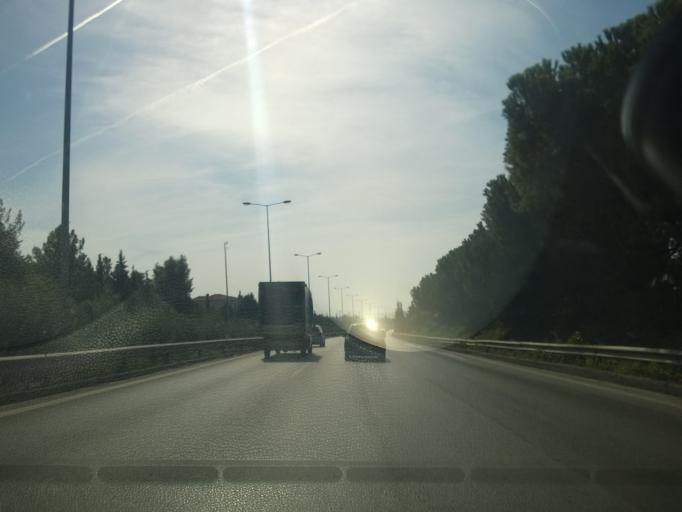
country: GR
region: Central Macedonia
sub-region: Nomos Thessalonikis
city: Pylaia
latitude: 40.5954
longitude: 22.9950
